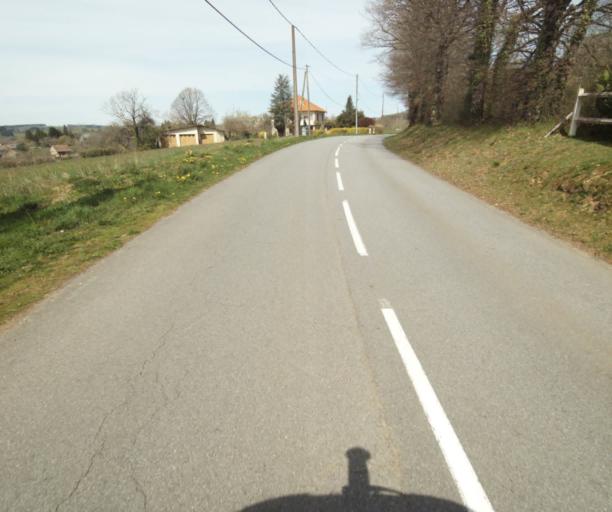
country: FR
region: Limousin
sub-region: Departement de la Correze
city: Correze
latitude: 45.3779
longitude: 1.8027
